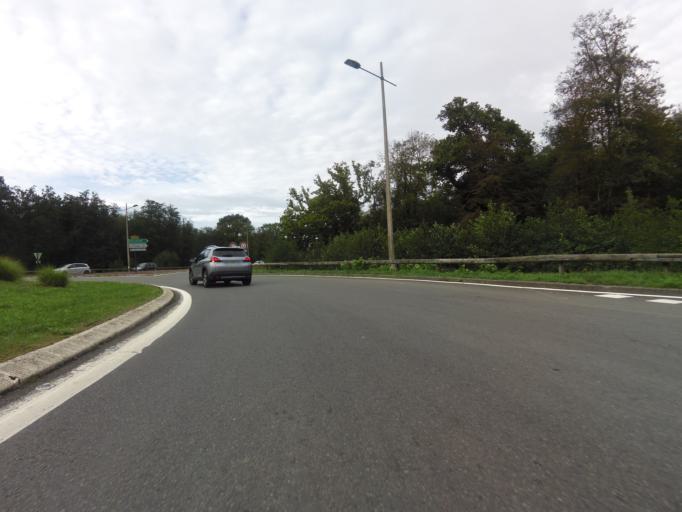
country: FR
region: Nord-Pas-de-Calais
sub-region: Departement du Pas-de-Calais
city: Condette
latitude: 50.6456
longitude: 1.6434
